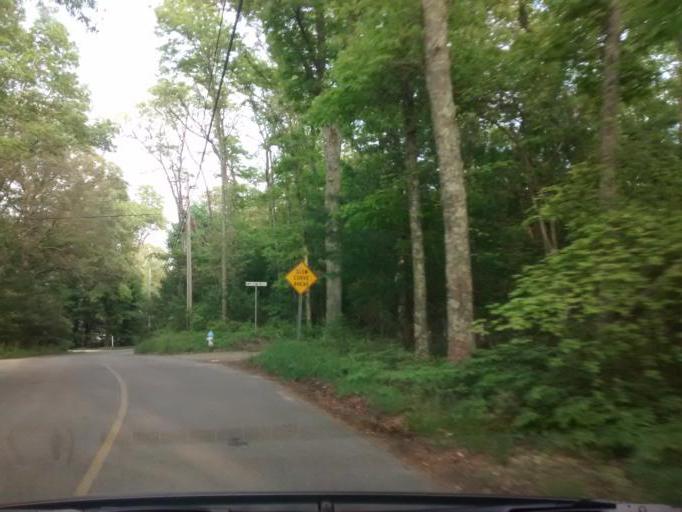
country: US
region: Massachusetts
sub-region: Barnstable County
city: Teaticket
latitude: 41.5920
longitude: -70.5903
